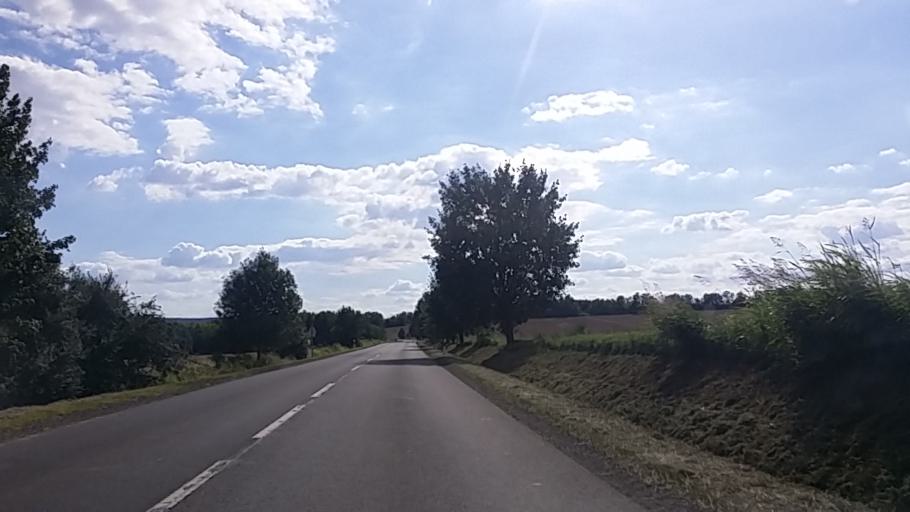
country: HU
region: Baranya
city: Sasd
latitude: 46.2848
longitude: 18.1160
